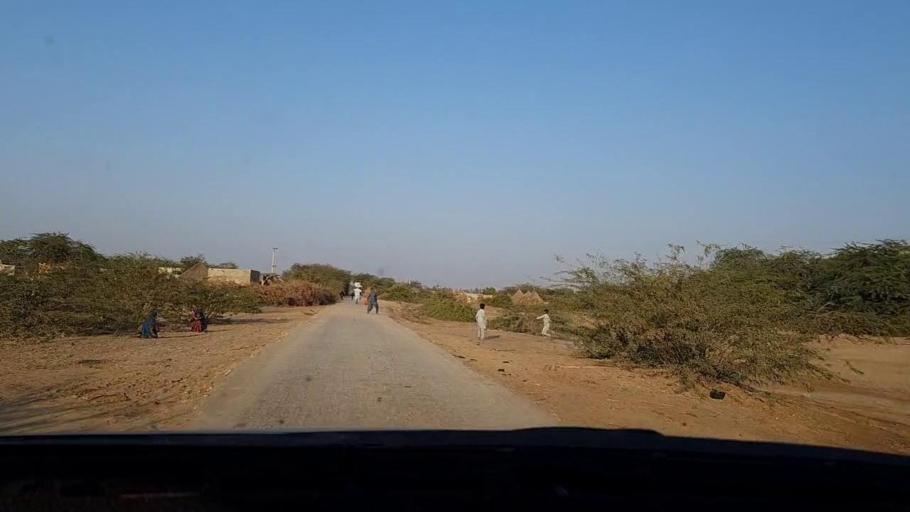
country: PK
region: Sindh
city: Tando Mittha Khan
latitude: 25.8687
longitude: 69.3091
